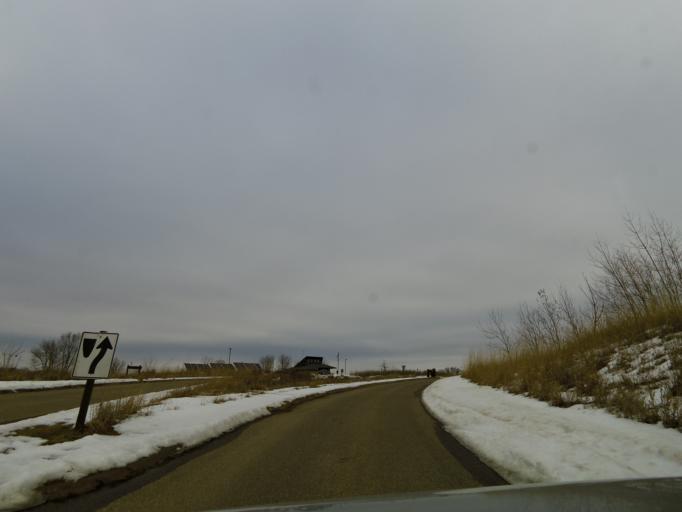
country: US
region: Minnesota
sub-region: Washington County
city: Afton
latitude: 44.8460
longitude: -92.7923
